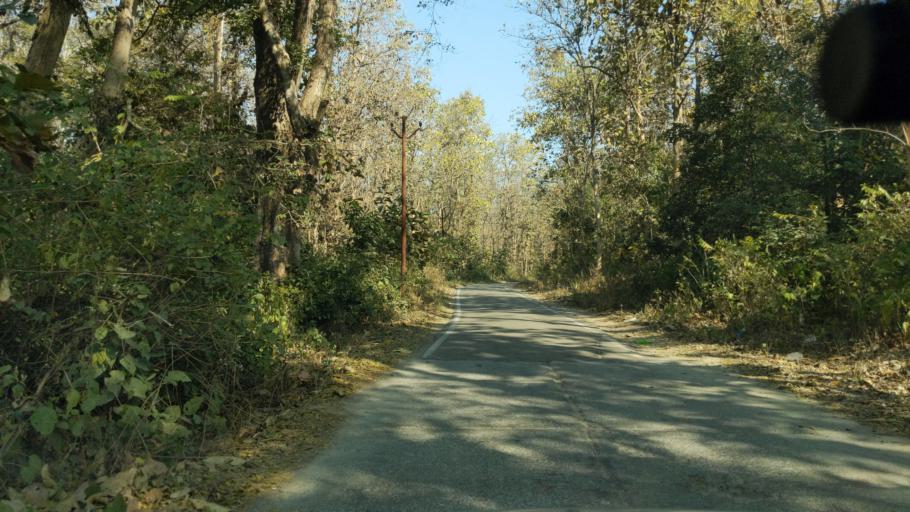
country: IN
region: Uttarakhand
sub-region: Naini Tal
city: Ramnagar
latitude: 29.4043
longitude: 79.1371
